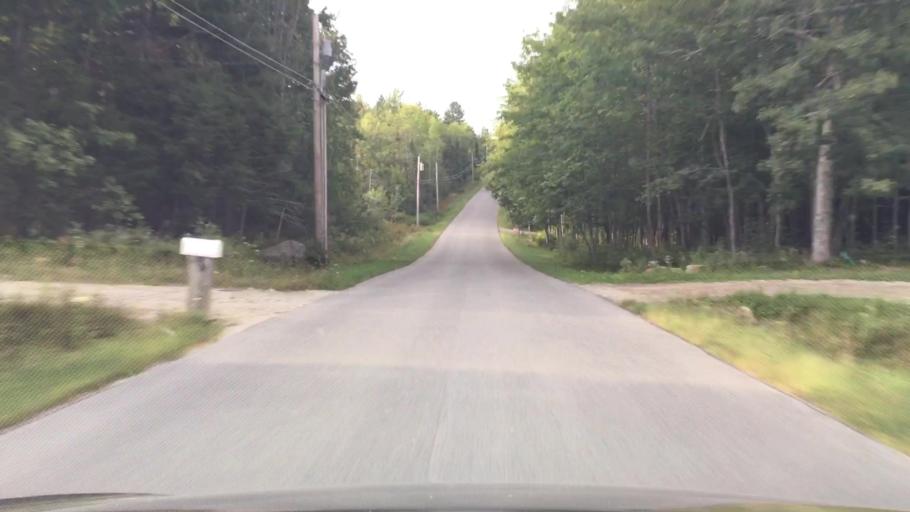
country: US
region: Maine
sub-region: Waldo County
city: Stockton Springs
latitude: 44.4979
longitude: -68.8745
